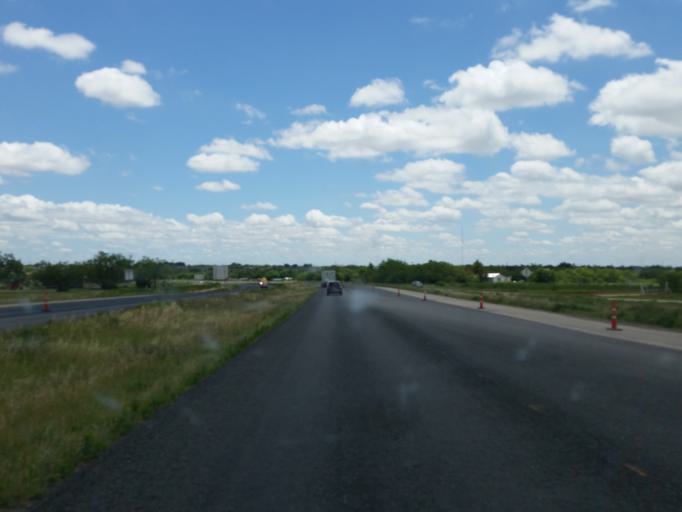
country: US
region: Texas
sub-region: Scurry County
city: Snyder
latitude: 32.7367
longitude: -100.9153
